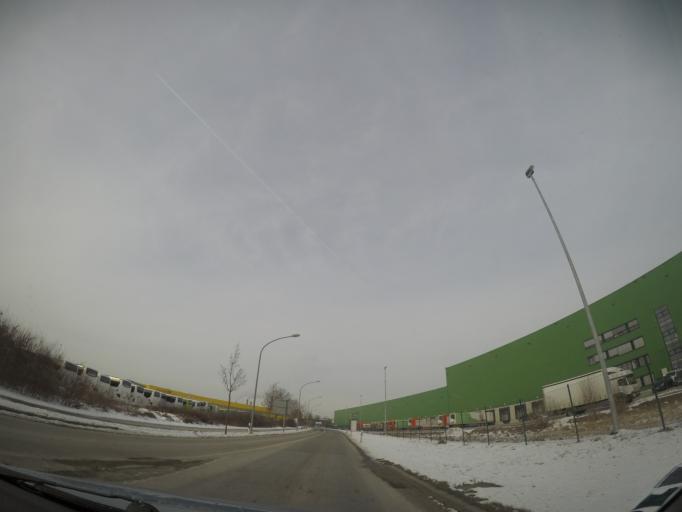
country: DE
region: Bavaria
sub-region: Swabia
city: Neu-Ulm
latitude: 48.3965
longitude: 10.0362
